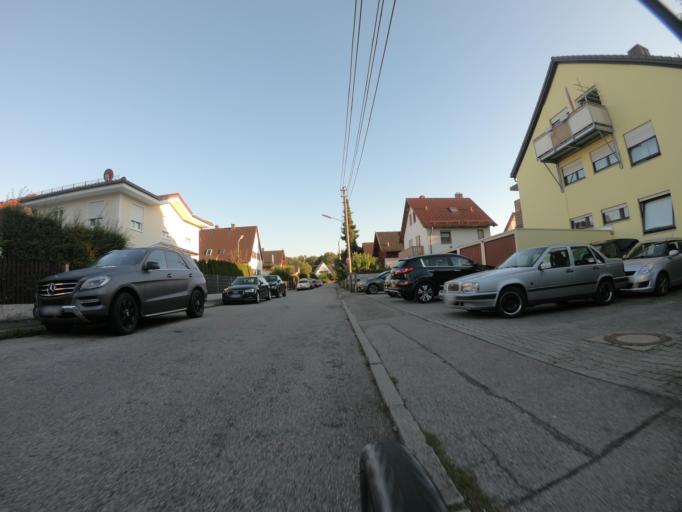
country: DE
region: Bavaria
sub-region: Upper Bavaria
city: Emmering
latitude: 48.1777
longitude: 11.2715
